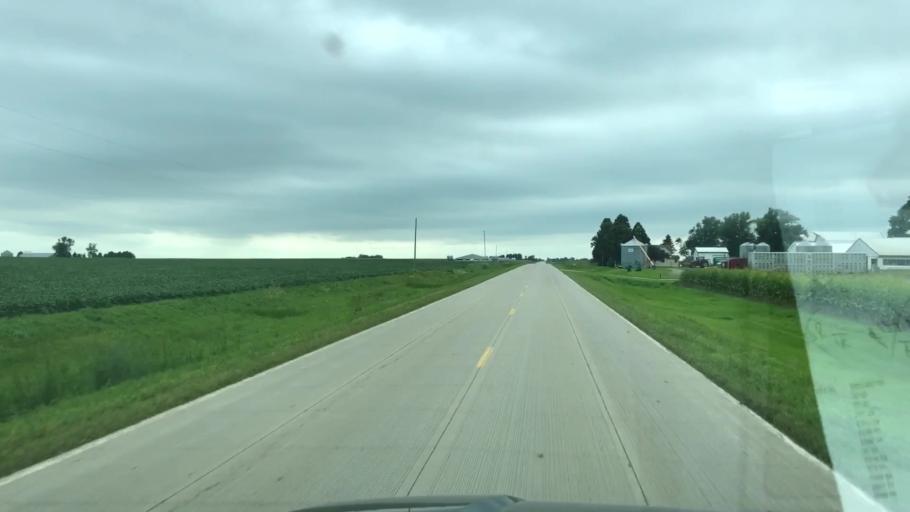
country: US
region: Iowa
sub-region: O'Brien County
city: Sheldon
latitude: 43.1344
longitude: -95.9792
